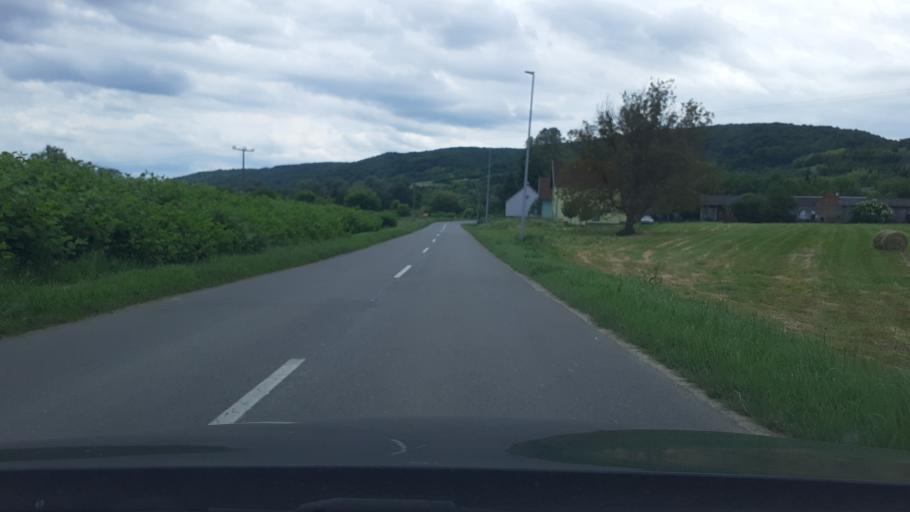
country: HR
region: Pozesko-Slavonska
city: Jaksic
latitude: 45.3304
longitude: 17.7558
